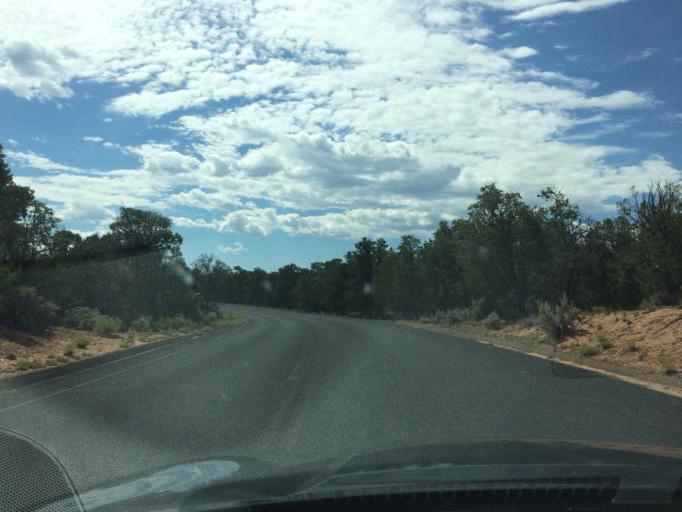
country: US
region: Arizona
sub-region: Apache County
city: Chinle
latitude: 36.1005
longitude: -109.3653
